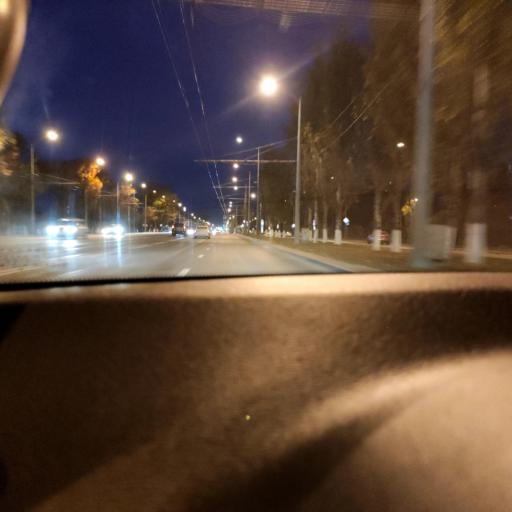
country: RU
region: Samara
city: Samara
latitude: 53.2349
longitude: 50.1999
